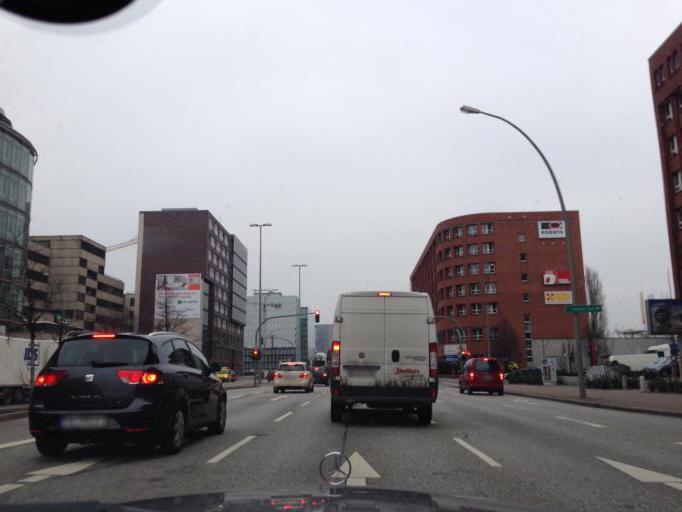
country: DE
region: Hamburg
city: Hammerbrook
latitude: 53.5448
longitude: 10.0311
